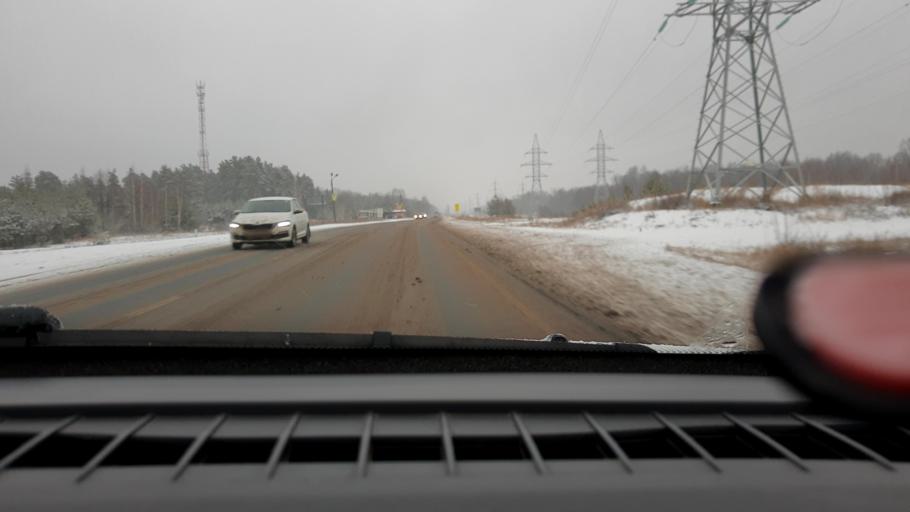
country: RU
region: Nizjnij Novgorod
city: Novaya Balakhna
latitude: 56.4702
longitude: 43.6139
